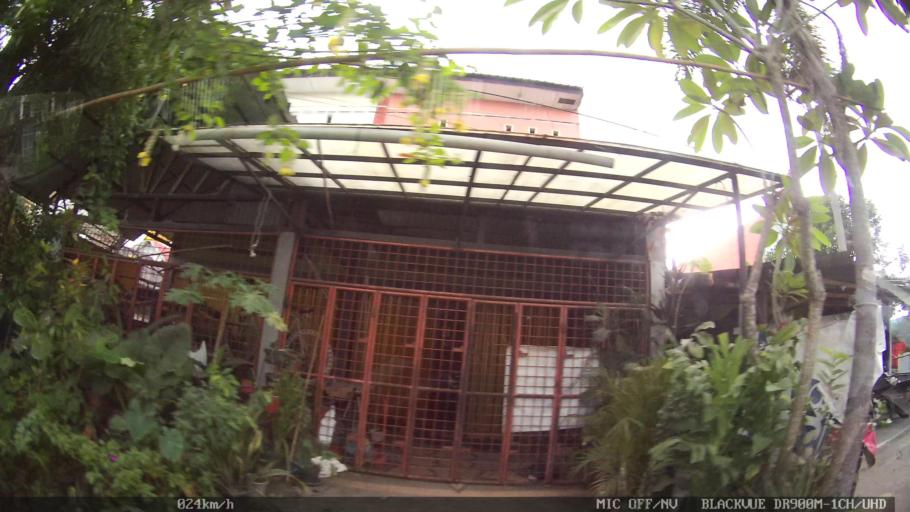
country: ID
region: North Sumatra
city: Sunggal
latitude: 3.5214
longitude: 98.6180
